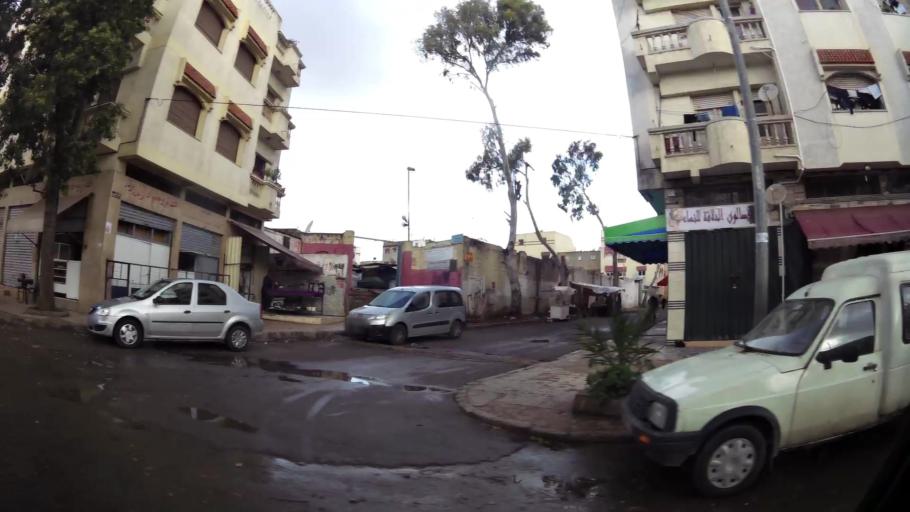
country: MA
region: Grand Casablanca
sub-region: Casablanca
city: Casablanca
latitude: 33.5612
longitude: -7.6796
